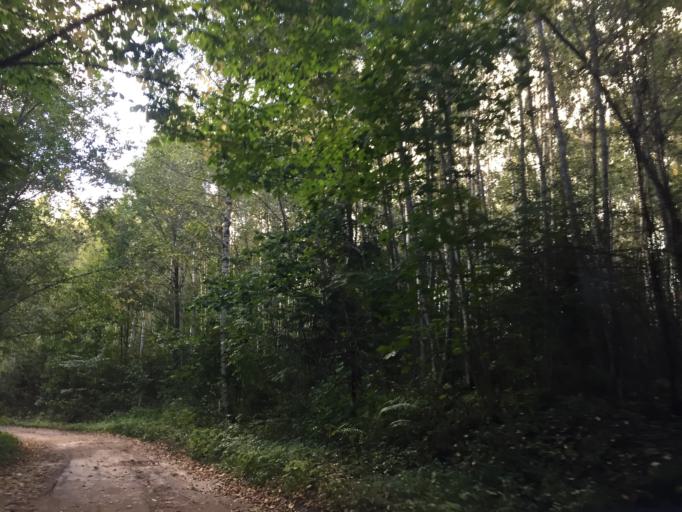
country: LV
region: Ligatne
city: Ligatne
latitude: 57.1232
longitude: 25.1338
